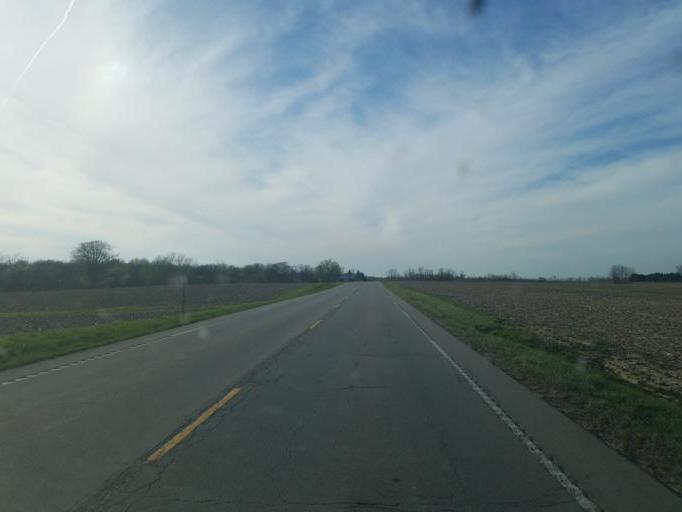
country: US
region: Ohio
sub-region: Huron County
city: New London
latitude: 41.0804
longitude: -82.4679
